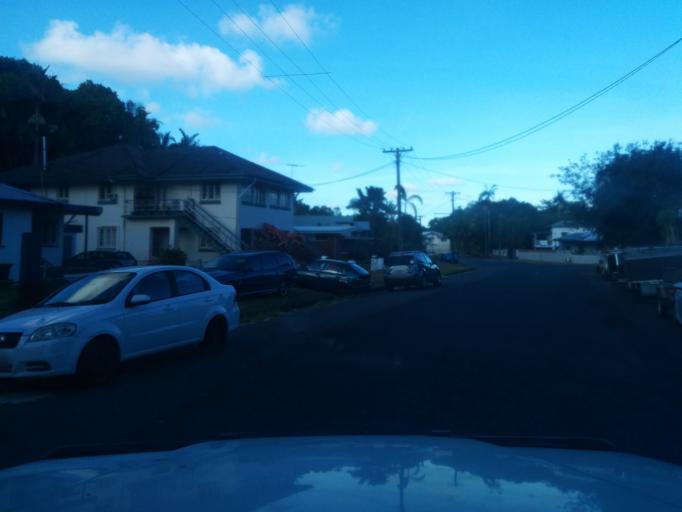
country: AU
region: Queensland
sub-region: Cairns
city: Woree
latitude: -16.9403
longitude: 145.7395
